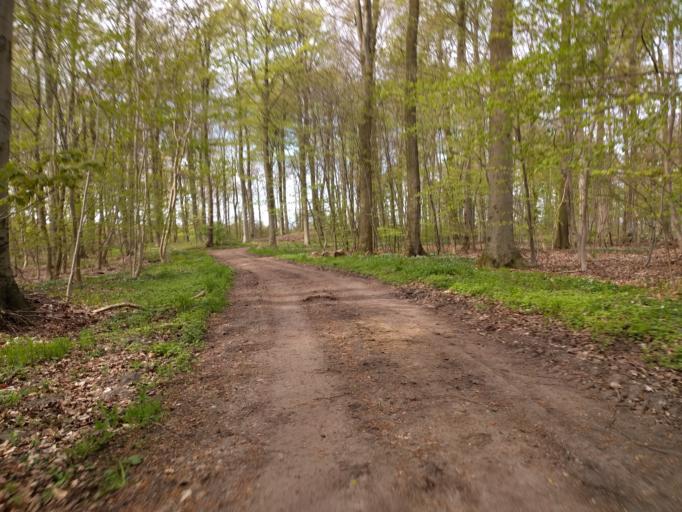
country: DK
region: South Denmark
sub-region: Kerteminde Kommune
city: Munkebo
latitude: 55.4319
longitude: 10.5542
